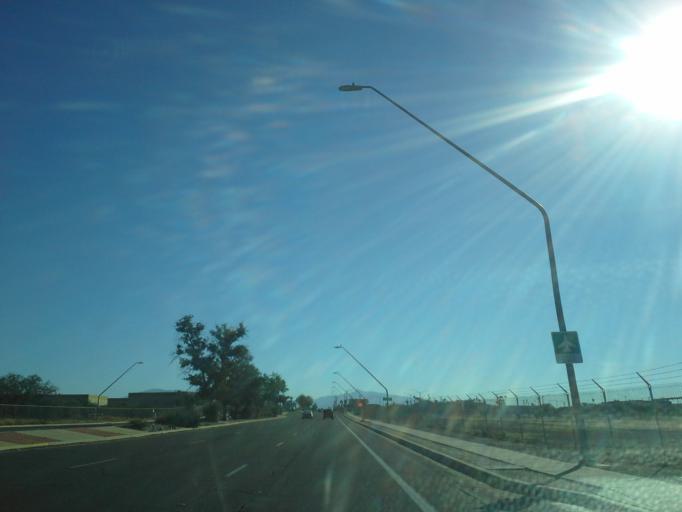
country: US
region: Arizona
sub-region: Pima County
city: Summit
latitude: 32.1340
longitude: -110.9416
